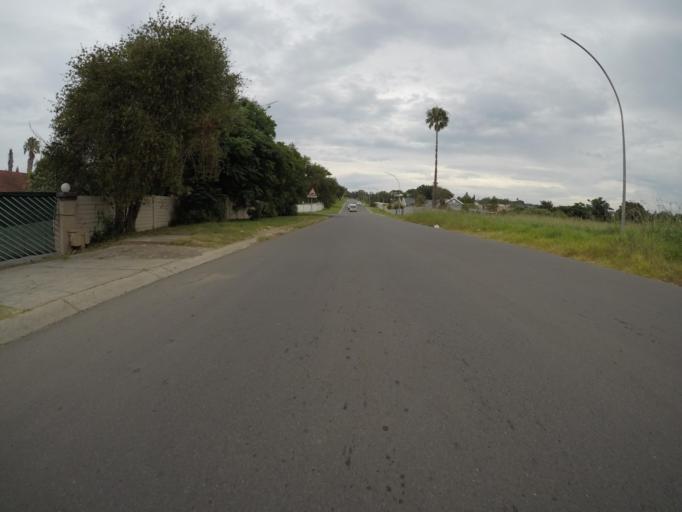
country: ZA
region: Eastern Cape
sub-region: Buffalo City Metropolitan Municipality
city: East London
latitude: -33.0019
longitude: 27.8578
